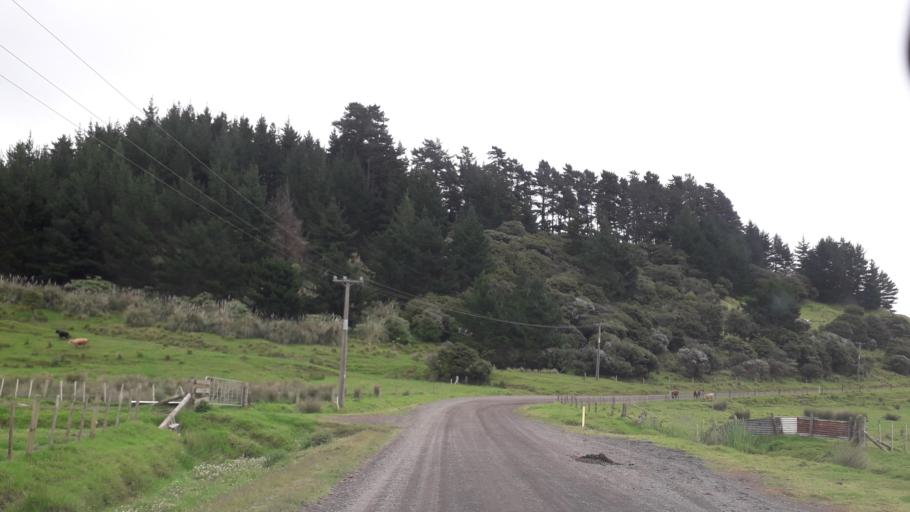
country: NZ
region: Northland
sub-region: Far North District
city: Ahipara
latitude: -35.4407
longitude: 173.3260
